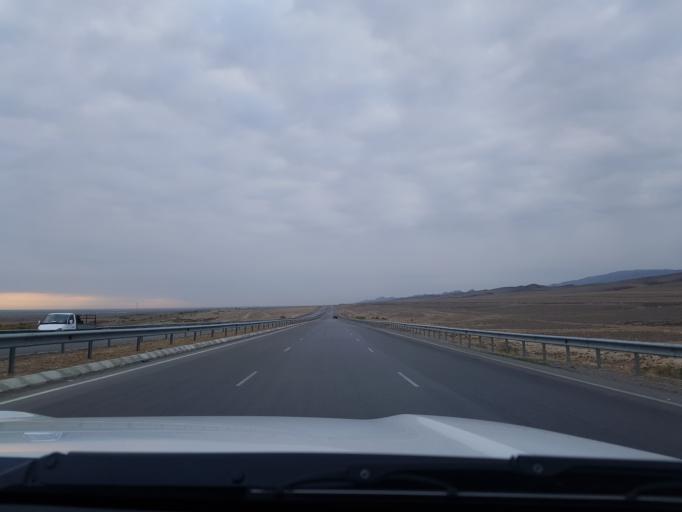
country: IR
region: Razavi Khorasan
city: Dargaz
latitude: 37.6816
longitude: 59.0844
